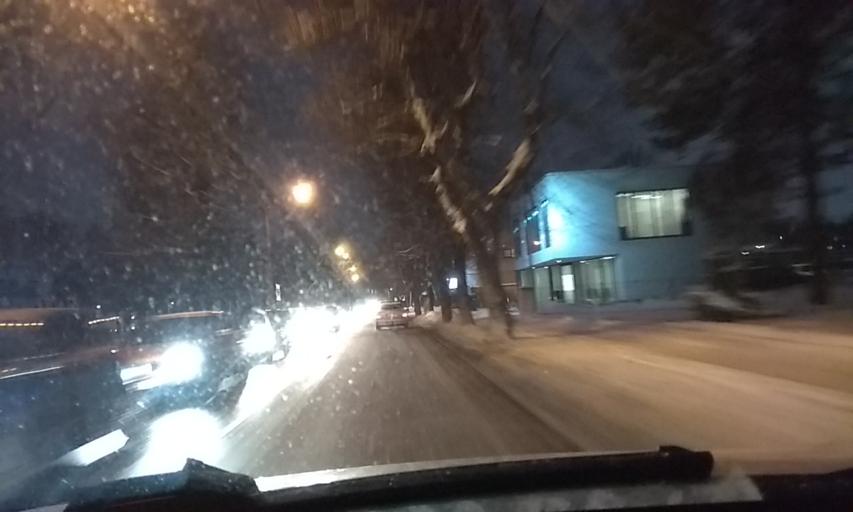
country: LT
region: Kauno apskritis
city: Dainava (Kaunas)
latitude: 54.9060
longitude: 23.9505
